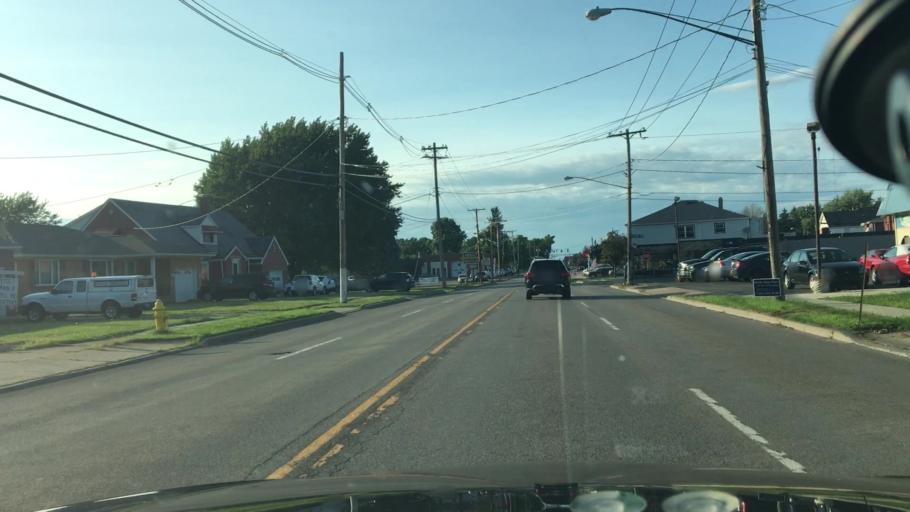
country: US
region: New York
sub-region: Erie County
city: Lackawanna
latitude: 42.8184
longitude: -78.8015
